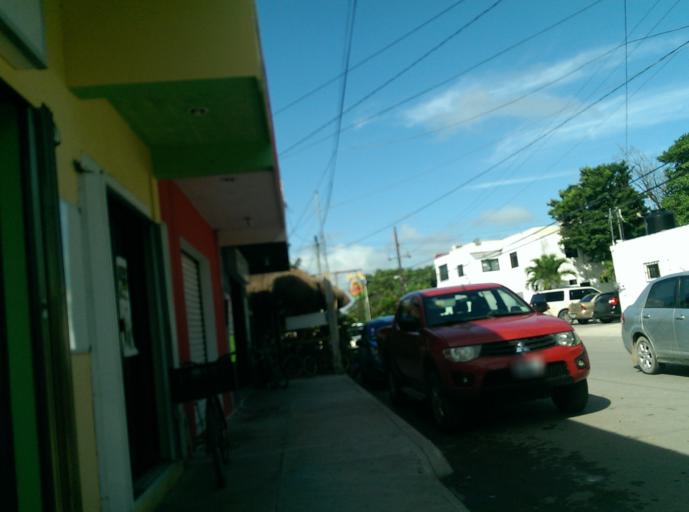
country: MX
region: Quintana Roo
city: Tulum
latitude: 20.2101
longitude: -87.4636
